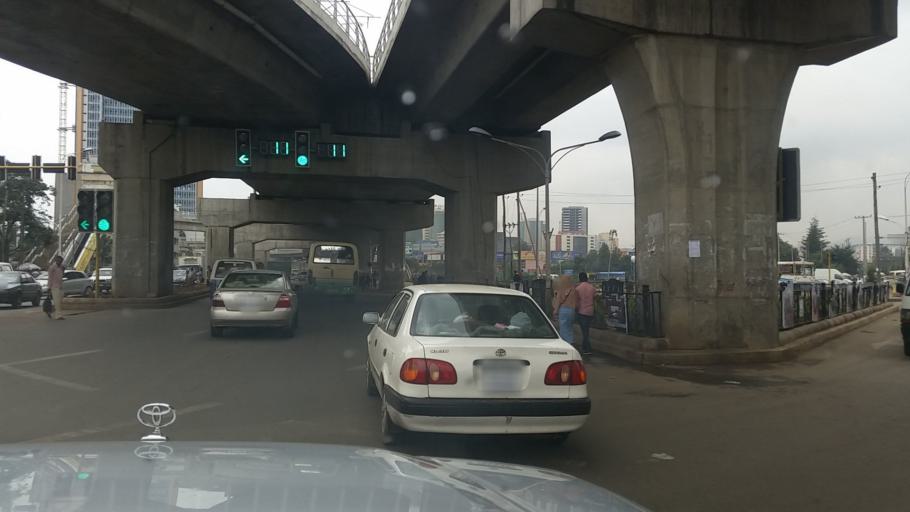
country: ET
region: Adis Abeba
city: Addis Ababa
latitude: 9.0116
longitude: 38.7594
